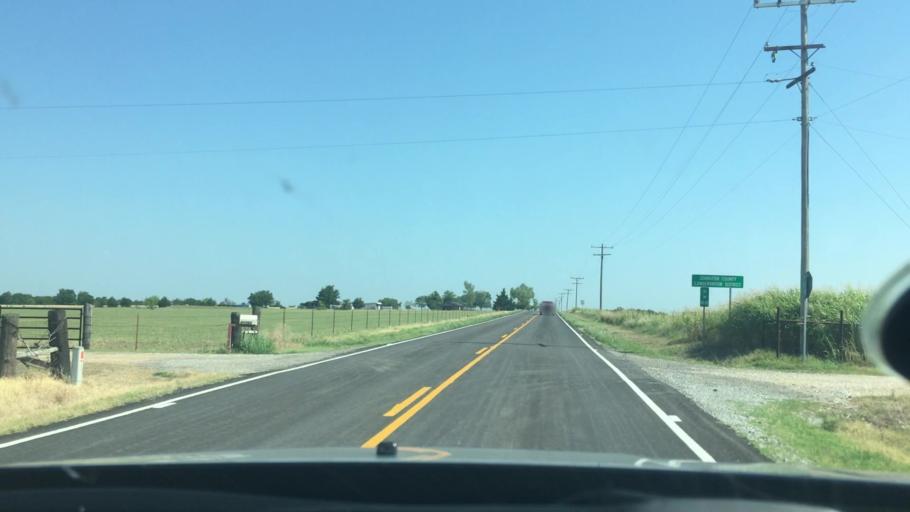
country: US
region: Oklahoma
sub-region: Bryan County
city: Durant
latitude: 34.1140
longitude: -96.4876
